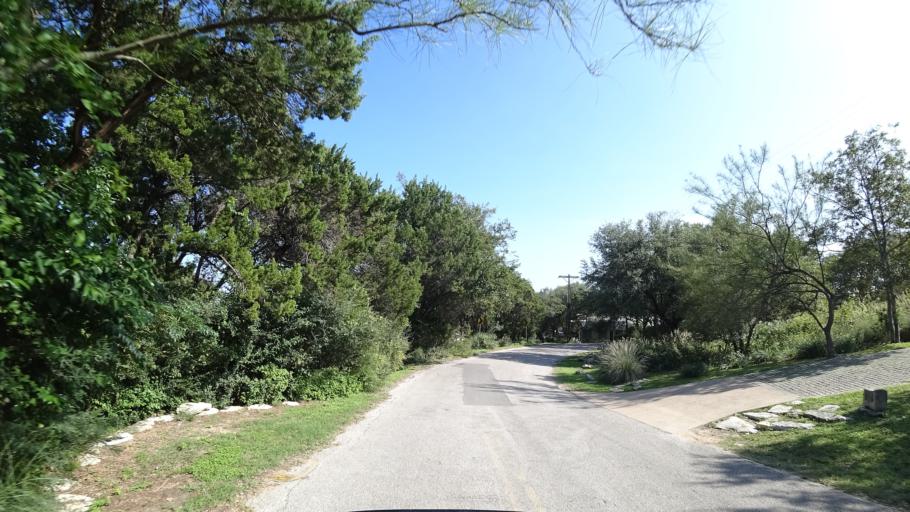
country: US
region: Texas
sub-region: Travis County
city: West Lake Hills
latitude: 30.2887
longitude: -97.8102
